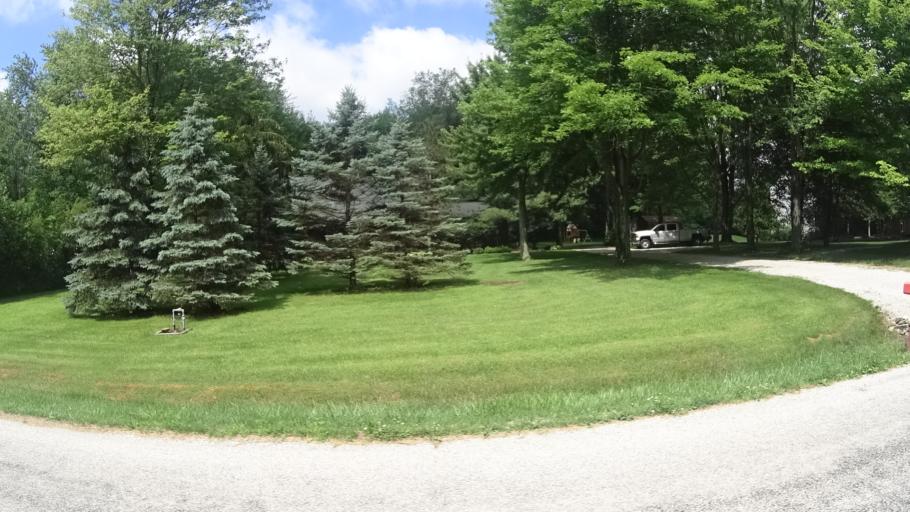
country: US
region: Ohio
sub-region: Huron County
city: Wakeman
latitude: 41.3088
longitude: -82.3634
